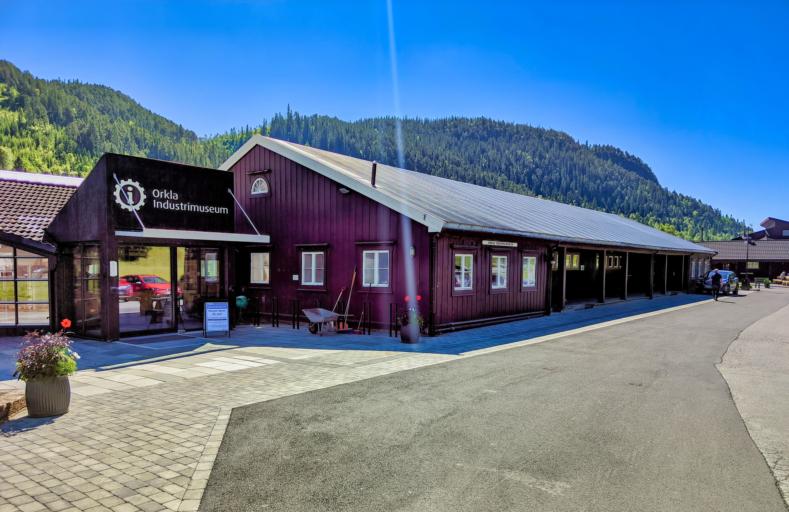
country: NO
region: Sor-Trondelag
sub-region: Meldal
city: Meldal
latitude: 63.1251
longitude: 9.7050
